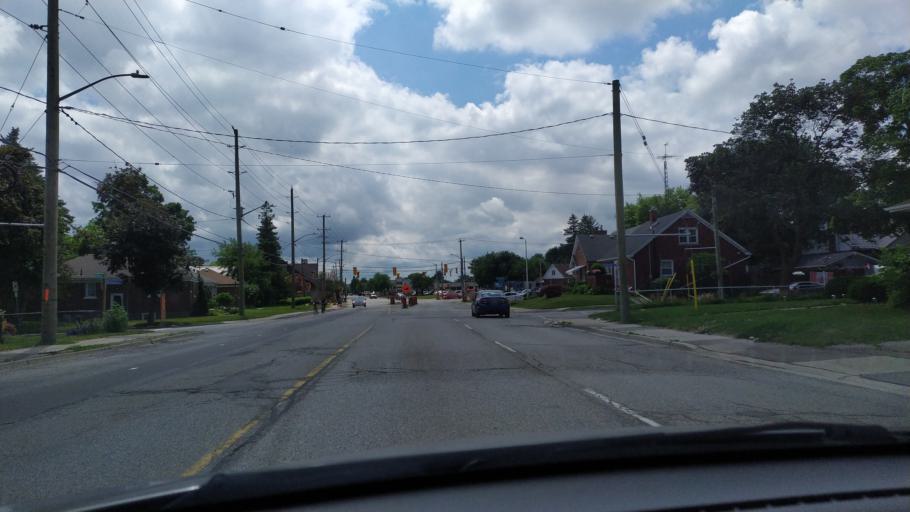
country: CA
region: Ontario
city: Kitchener
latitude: 43.4447
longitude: -80.4656
